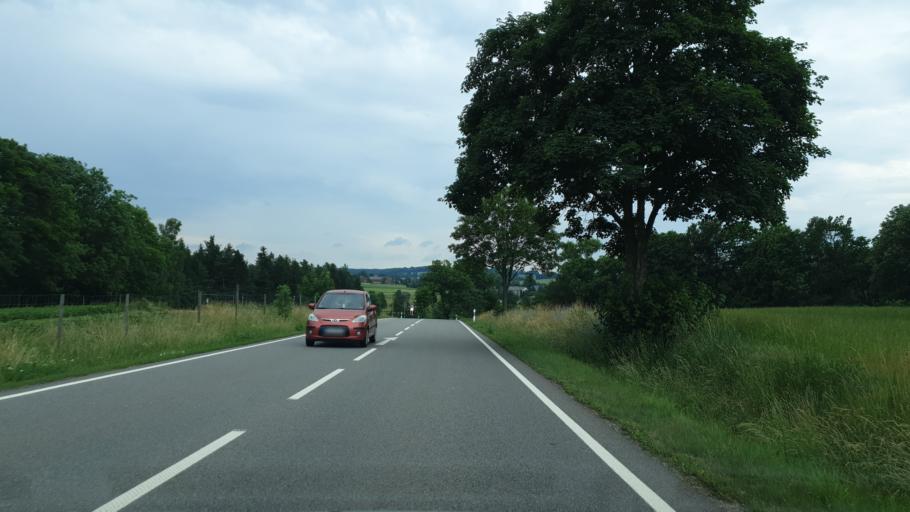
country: DE
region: Saxony
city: Hirschfeld
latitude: 50.6194
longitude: 12.4313
